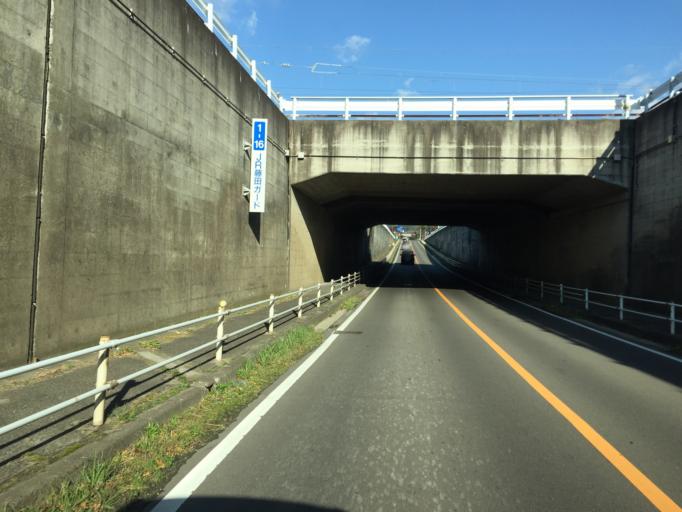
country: JP
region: Fukushima
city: Hobaramachi
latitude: 37.8768
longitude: 140.5371
